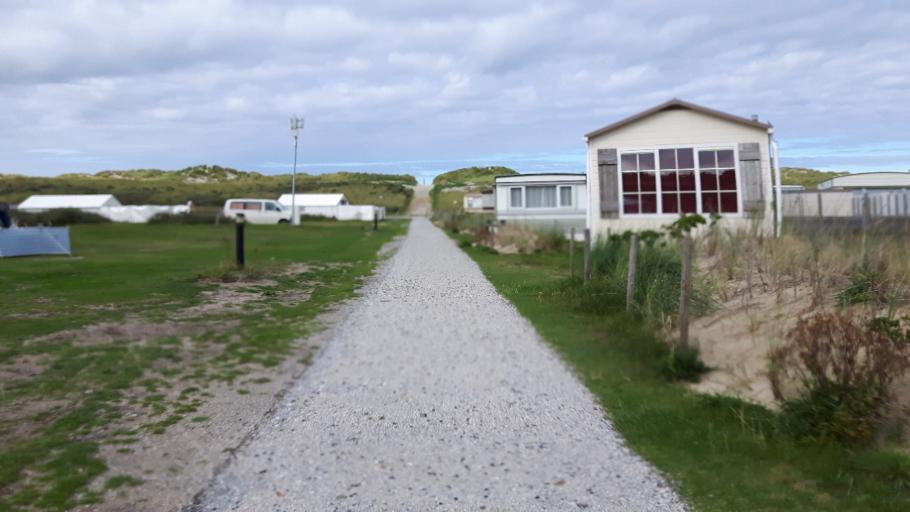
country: NL
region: Friesland
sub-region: Gemeente Ameland
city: Nes
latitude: 53.4574
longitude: 5.7677
